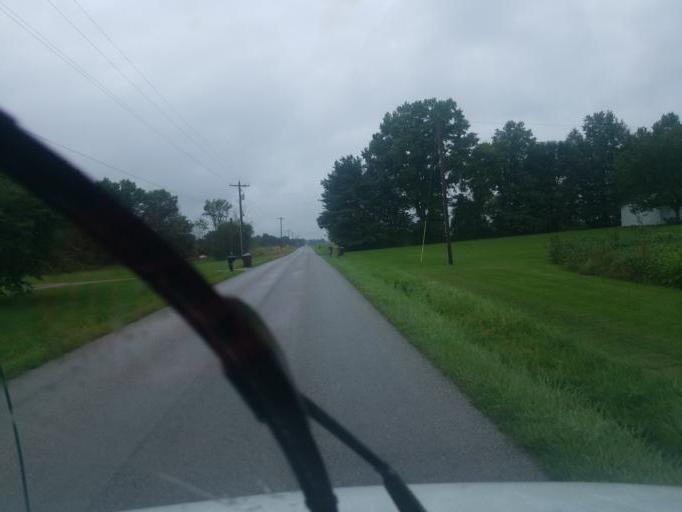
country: US
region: Ohio
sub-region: Wayne County
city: Creston
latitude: 40.9742
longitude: -81.9419
